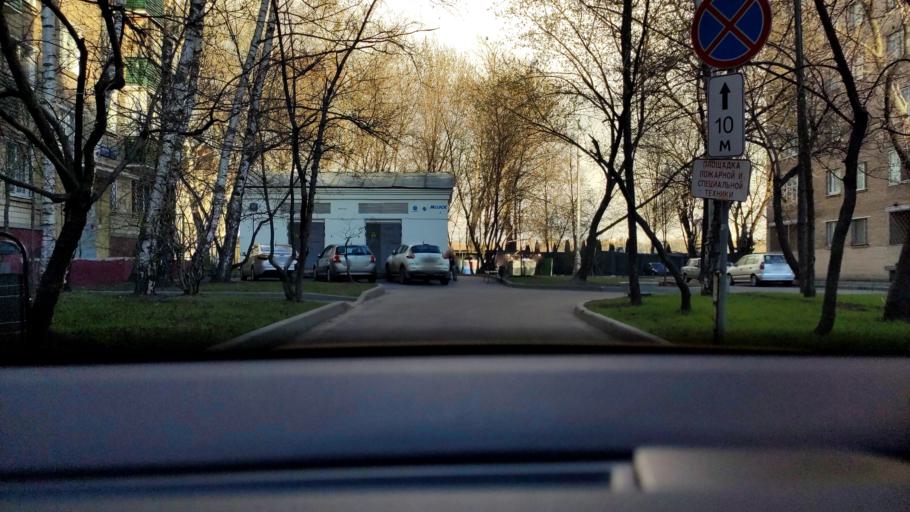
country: RU
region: Moskovskaya
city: Presnenskiy
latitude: 55.7775
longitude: 37.5575
